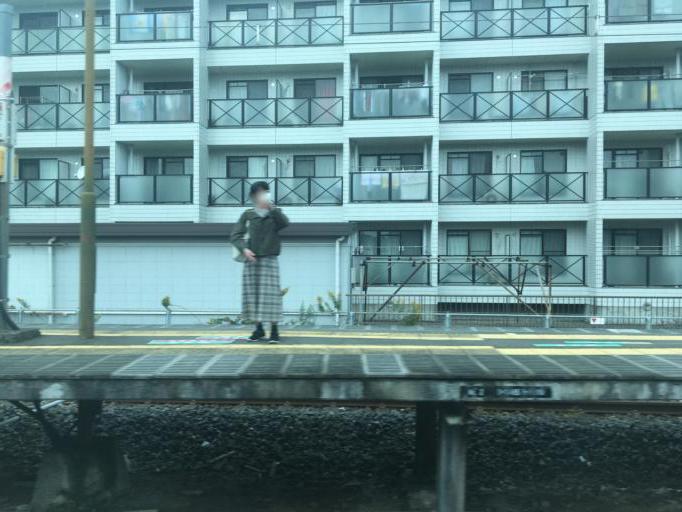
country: JP
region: Saitama
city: Kamifukuoka
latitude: 35.9034
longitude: 139.5208
